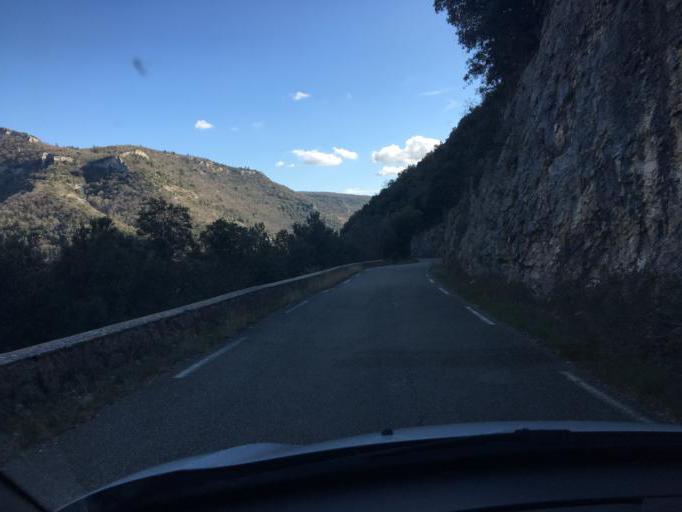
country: FR
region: Provence-Alpes-Cote d'Azur
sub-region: Departement du Vaucluse
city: Villes-sur-Auzon
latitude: 44.0689
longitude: 5.3051
